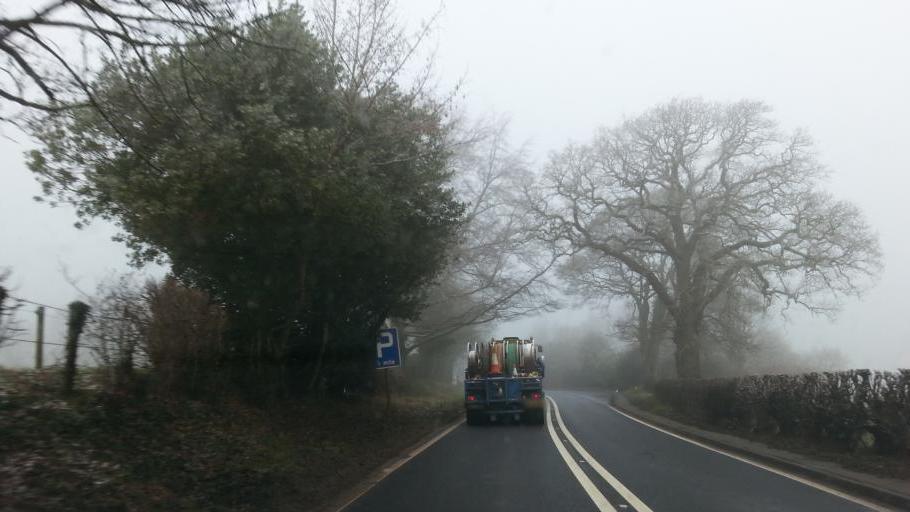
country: GB
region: England
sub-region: Cheshire East
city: Siddington
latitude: 53.2165
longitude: -2.2331
